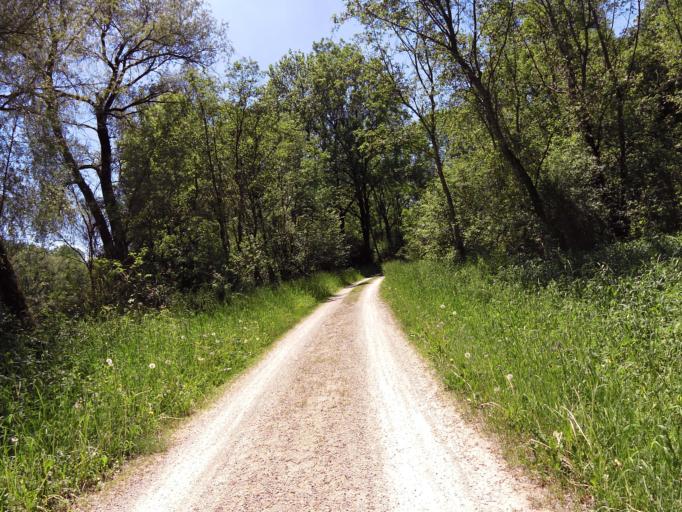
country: DE
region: Bavaria
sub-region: Upper Bavaria
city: Hallbergmoos
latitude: 48.3280
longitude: 11.7071
